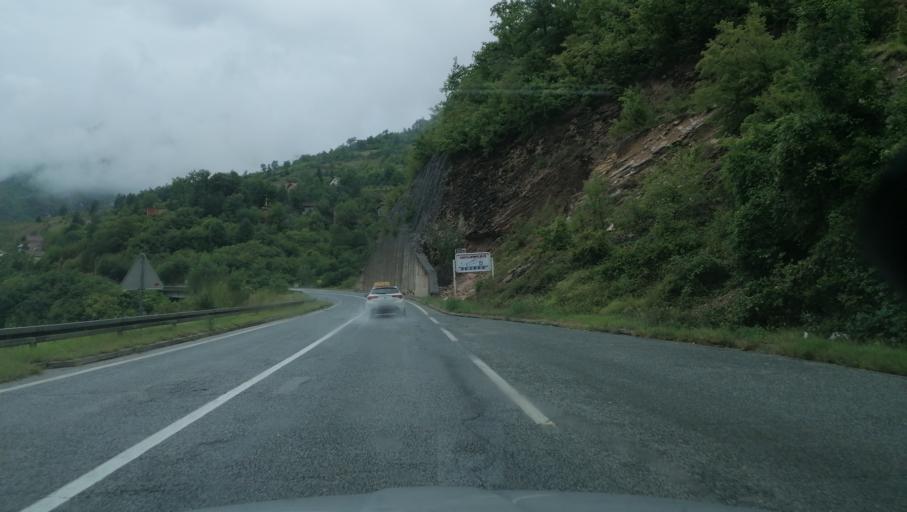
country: BA
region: Republika Srpska
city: Visegrad
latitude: 43.7327
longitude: 19.1851
